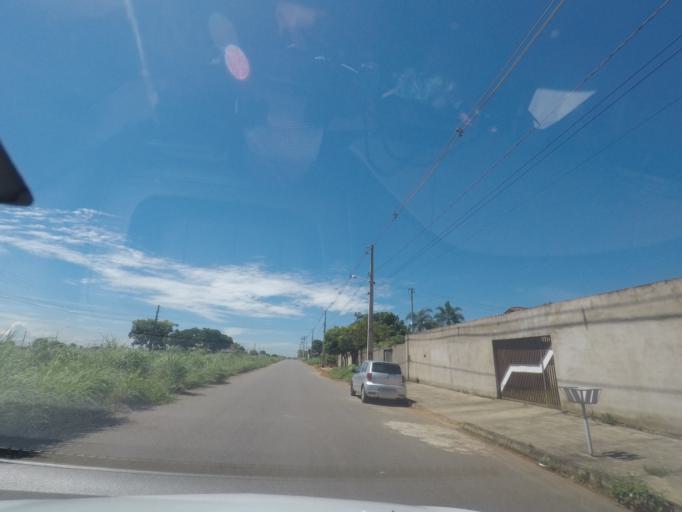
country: BR
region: Goias
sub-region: Aparecida De Goiania
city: Aparecida de Goiania
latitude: -16.7865
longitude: -49.3320
